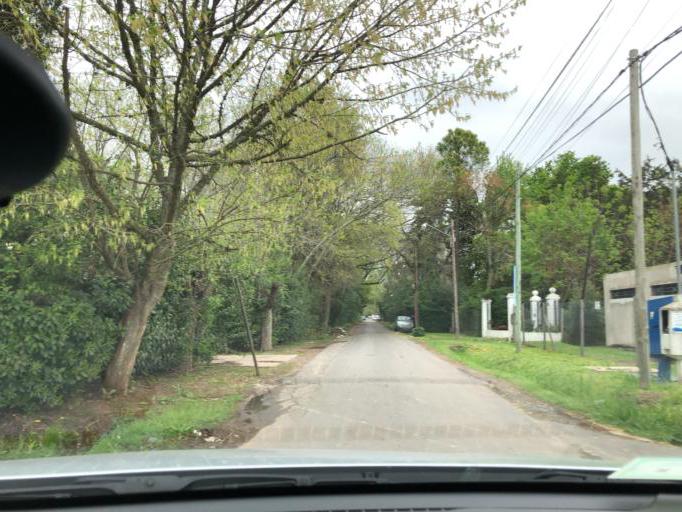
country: AR
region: Buenos Aires
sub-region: Partido de La Plata
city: La Plata
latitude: -34.8721
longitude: -58.0833
